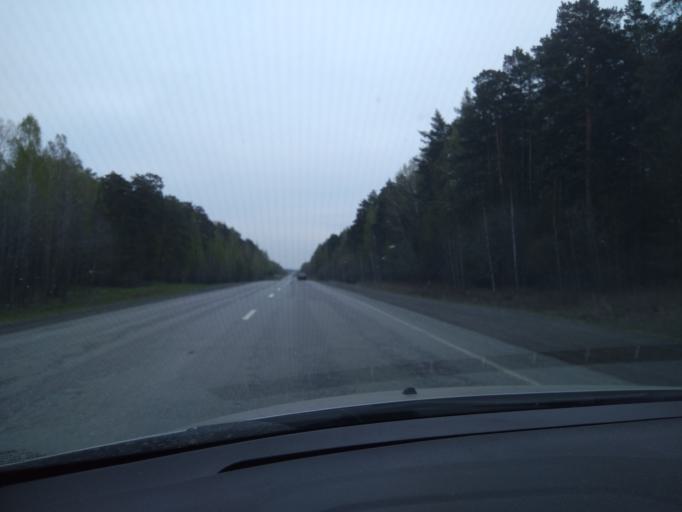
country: RU
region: Sverdlovsk
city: Baraba
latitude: 56.7803
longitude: 61.7894
